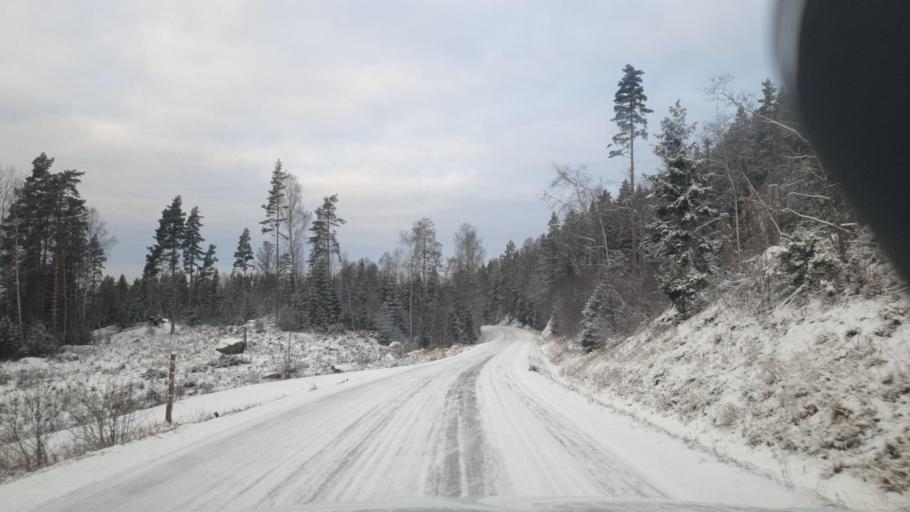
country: NO
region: Hedmark
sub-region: Eidskog
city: Skotterud
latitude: 59.8040
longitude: 12.0357
